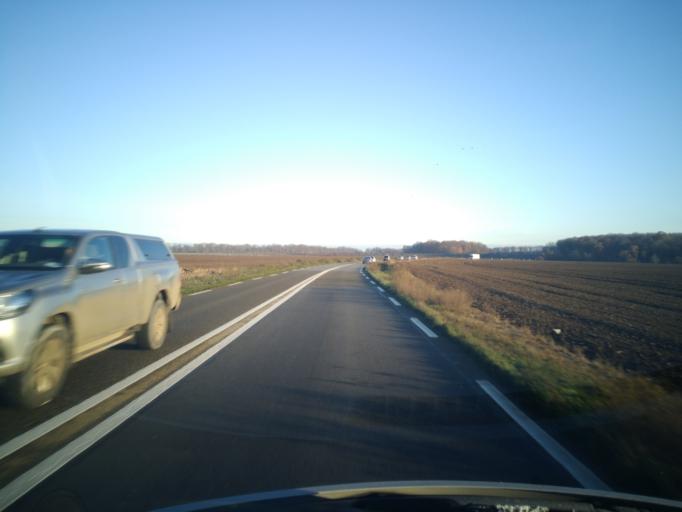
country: FR
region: Ile-de-France
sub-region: Departement des Yvelines
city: Feucherolles
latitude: 48.8793
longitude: 1.9836
